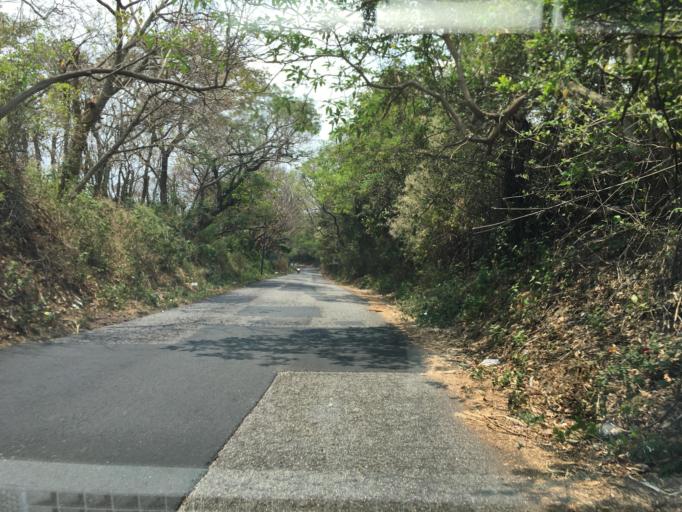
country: GT
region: Escuintla
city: San Vicente Pacaya
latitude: 14.3853
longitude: -90.5528
